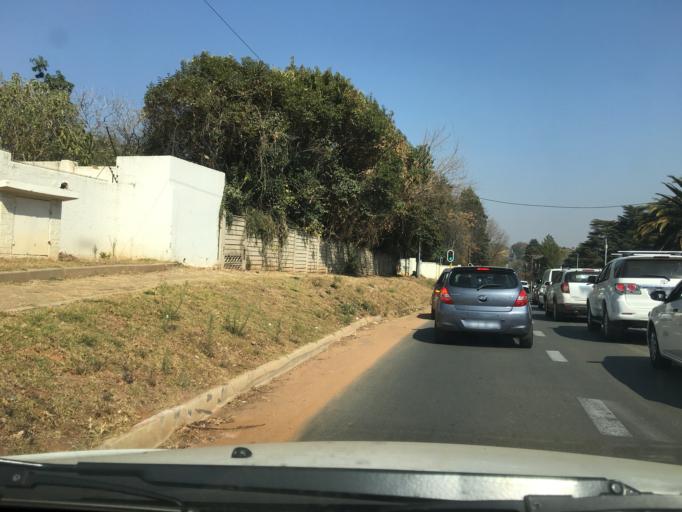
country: ZA
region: Gauteng
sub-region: City of Johannesburg Metropolitan Municipality
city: Midrand
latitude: -26.0640
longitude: 28.0540
